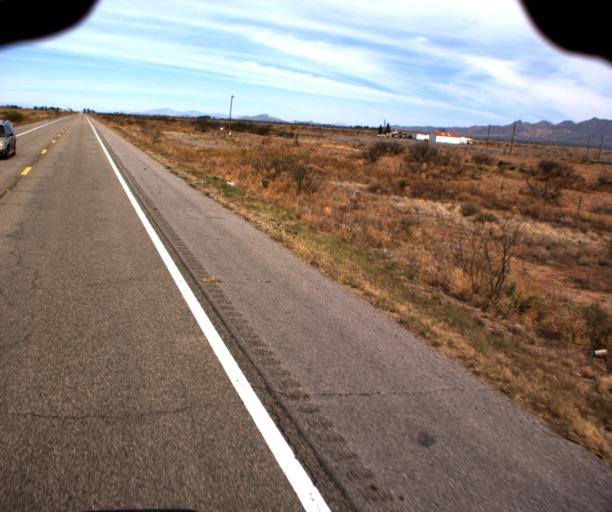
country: US
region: Arizona
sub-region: Cochise County
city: Pirtleville
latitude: 31.5751
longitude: -109.6683
